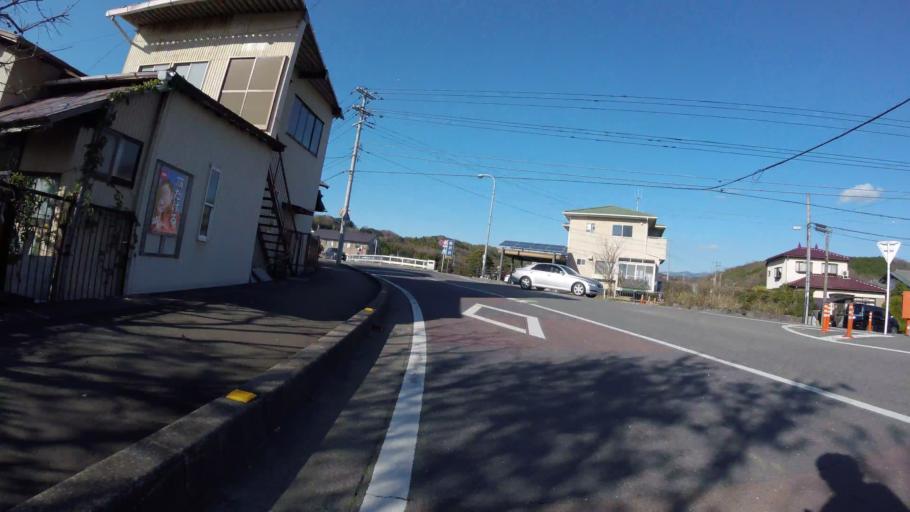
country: JP
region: Shizuoka
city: Mishima
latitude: 35.0867
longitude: 138.9682
